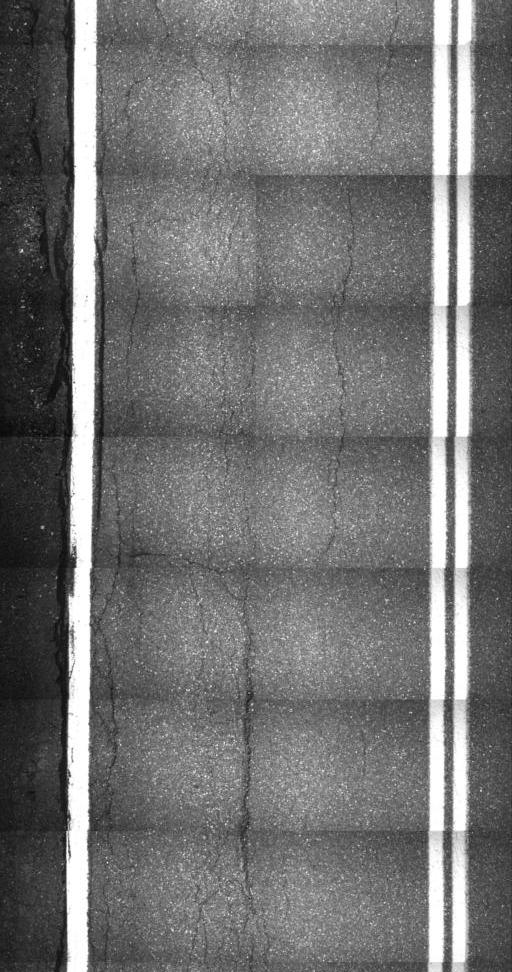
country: US
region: Massachusetts
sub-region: Franklin County
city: Colrain
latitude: 42.7472
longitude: -72.7448
